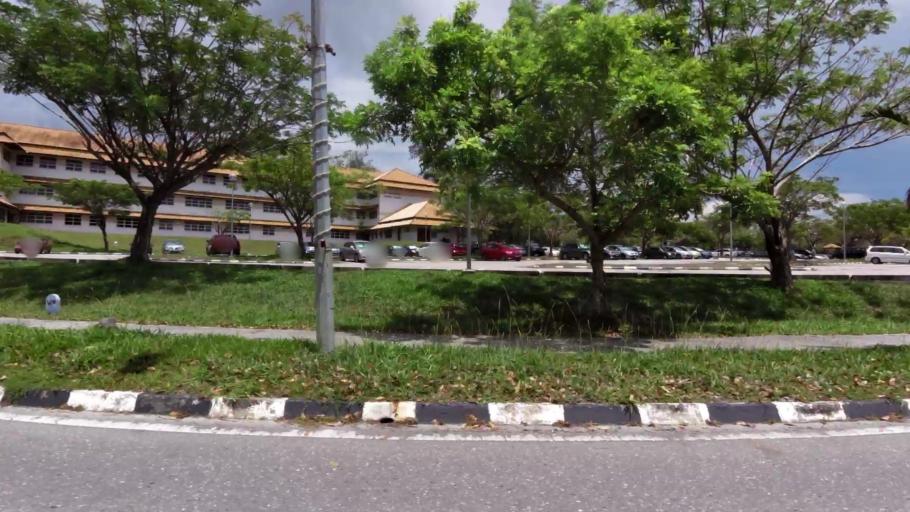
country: BN
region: Brunei and Muara
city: Bandar Seri Begawan
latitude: 4.9769
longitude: 114.8929
